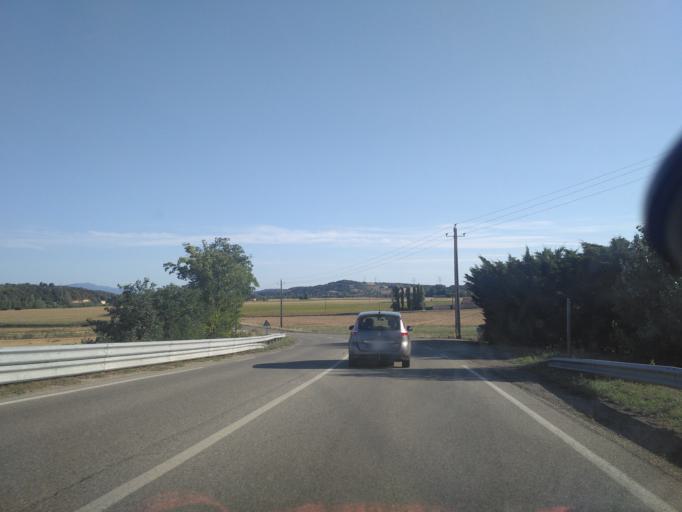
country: FR
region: Rhone-Alpes
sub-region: Departement de la Drome
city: Clerieux
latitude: 45.0798
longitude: 4.9581
